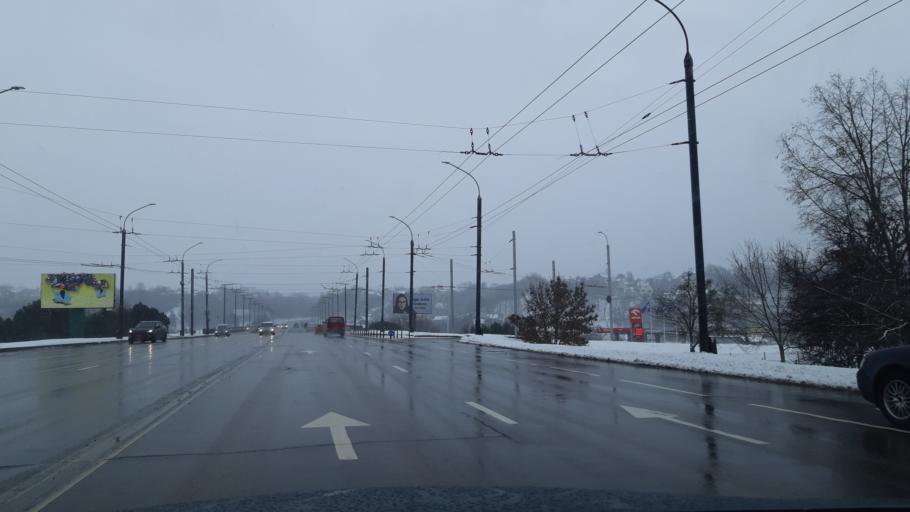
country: LT
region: Kauno apskritis
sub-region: Kaunas
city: Kaunas
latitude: 54.9146
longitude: 23.9052
